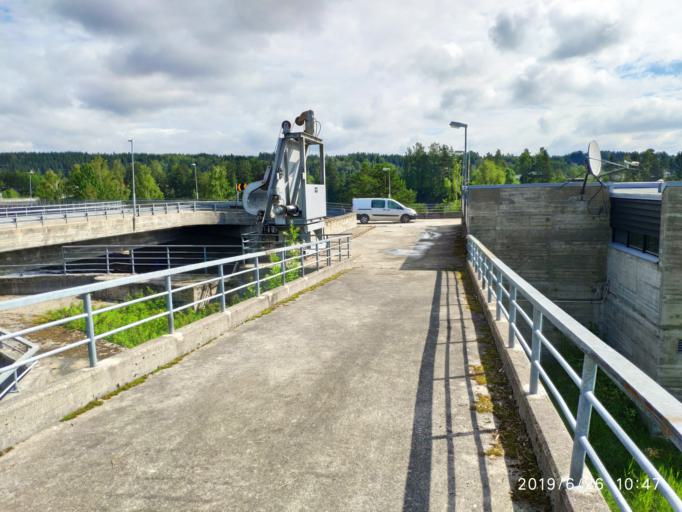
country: NO
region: Hedmark
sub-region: Elverum
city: Elverum
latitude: 60.8305
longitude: 11.6113
